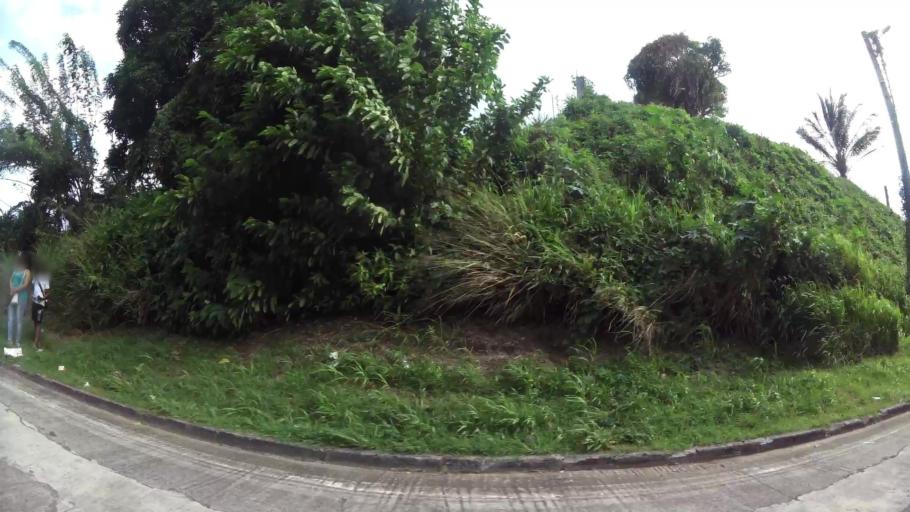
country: MQ
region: Martinique
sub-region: Martinique
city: Le Lorrain
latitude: 14.8166
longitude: -61.0252
